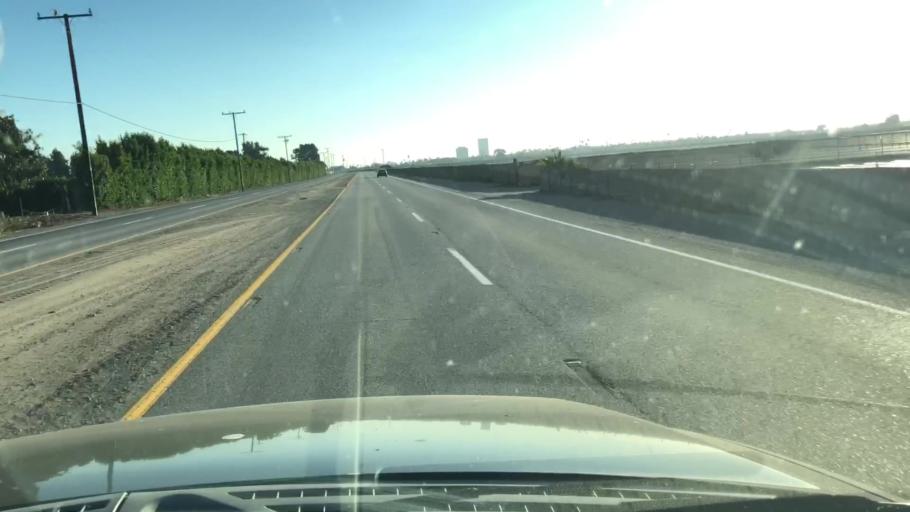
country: US
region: California
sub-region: Ventura County
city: El Rio
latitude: 34.2484
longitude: -119.1454
